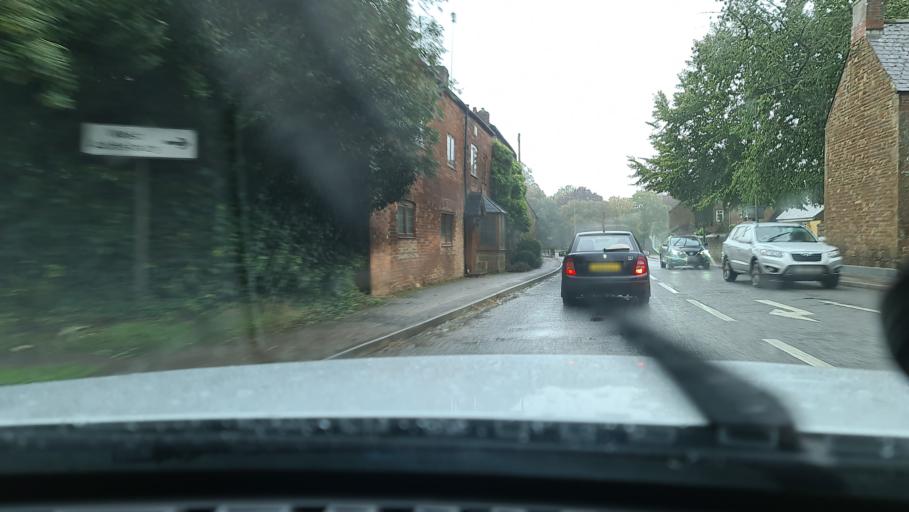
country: GB
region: England
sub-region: Oxfordshire
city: Adderbury
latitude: 52.0187
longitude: -1.3105
